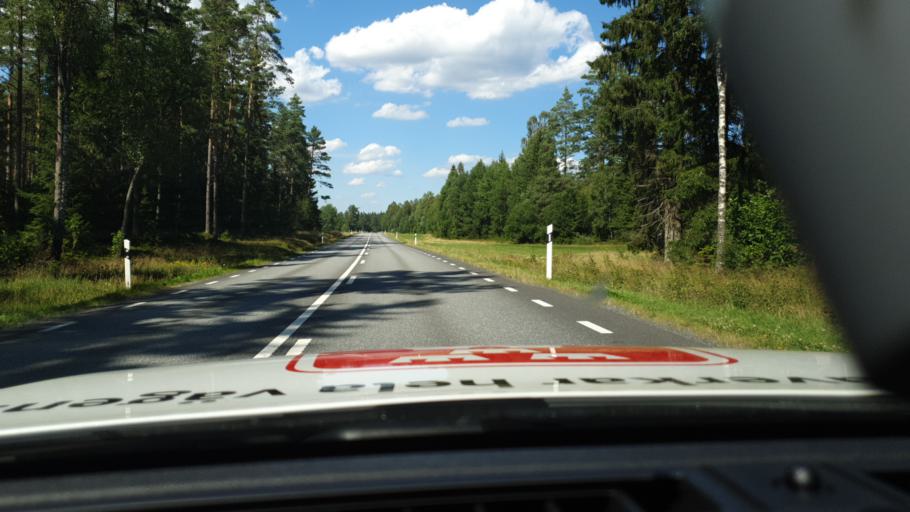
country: SE
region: Joenkoeping
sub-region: Savsjo Kommun
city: Vrigstad
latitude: 57.4461
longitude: 14.3199
